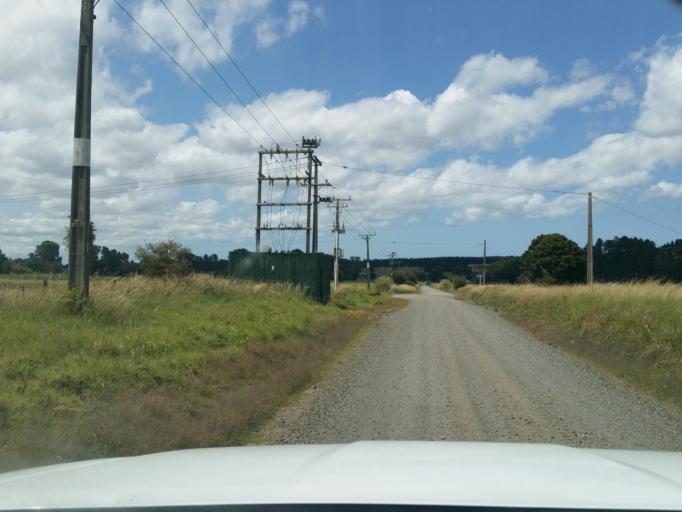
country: NZ
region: Northland
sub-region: Kaipara District
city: Dargaville
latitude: -35.7982
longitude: 173.7316
